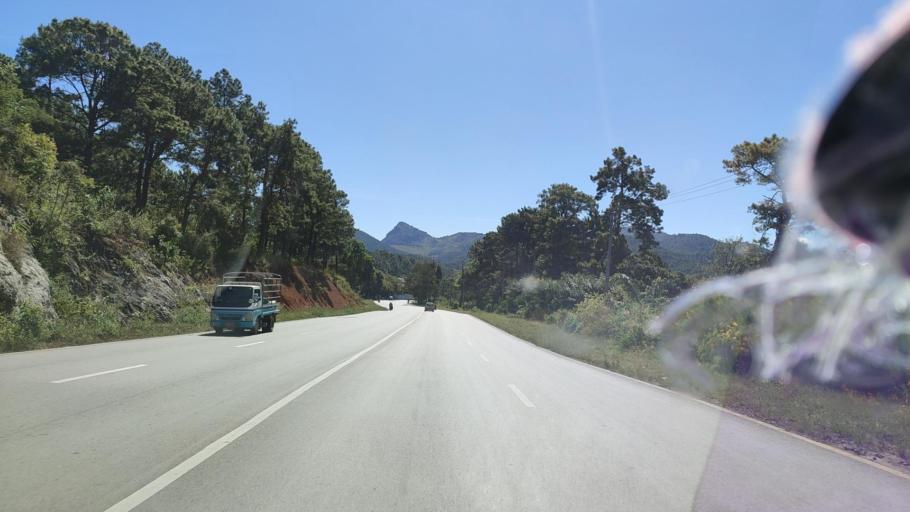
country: MM
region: Shan
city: Taunggyi
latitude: 20.6473
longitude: 96.5916
